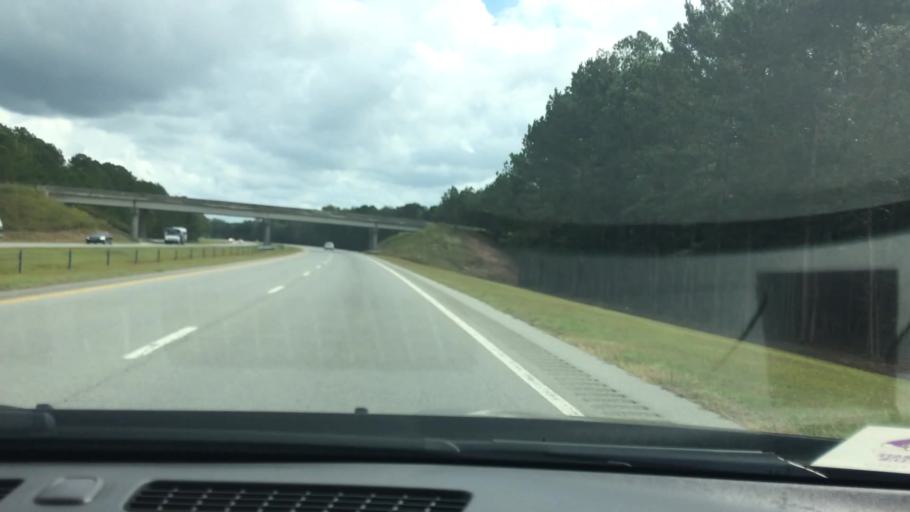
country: US
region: North Carolina
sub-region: Pitt County
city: Farmville
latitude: 35.6238
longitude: -77.7090
